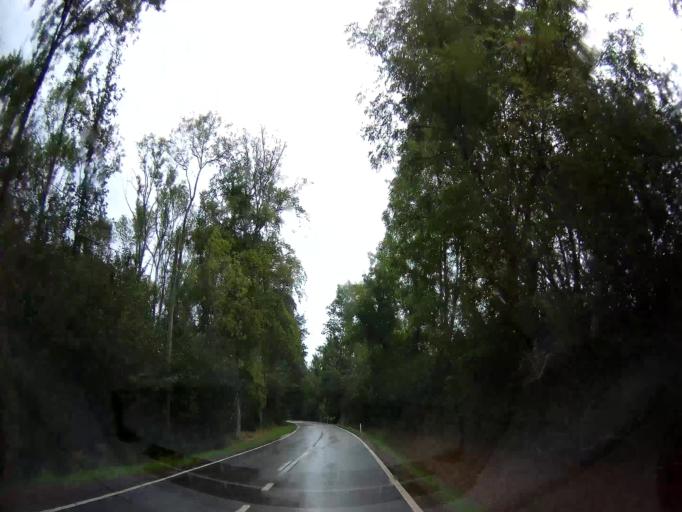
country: BE
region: Wallonia
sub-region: Province de Liege
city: Ferrieres
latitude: 50.4264
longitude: 5.6020
